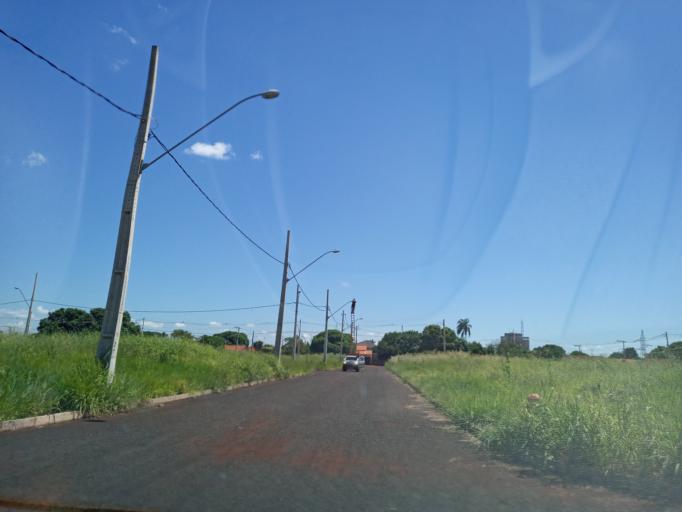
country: BR
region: Minas Gerais
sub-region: Centralina
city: Centralina
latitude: -18.5958
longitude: -49.1976
